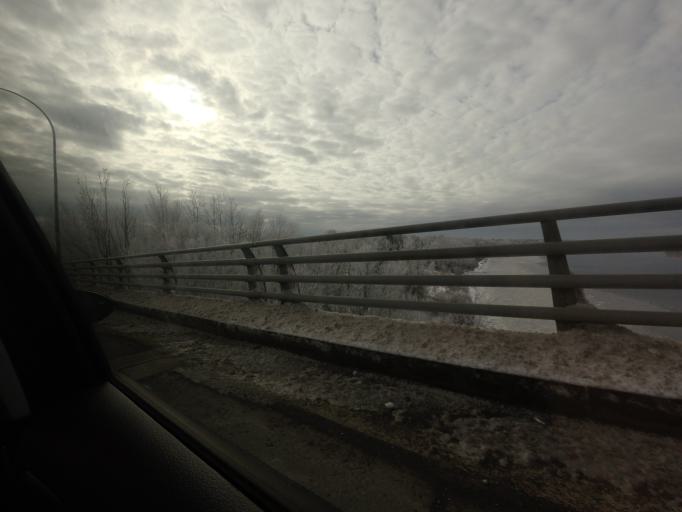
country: CA
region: New Brunswick
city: Oromocto
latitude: 45.8629
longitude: -66.4497
